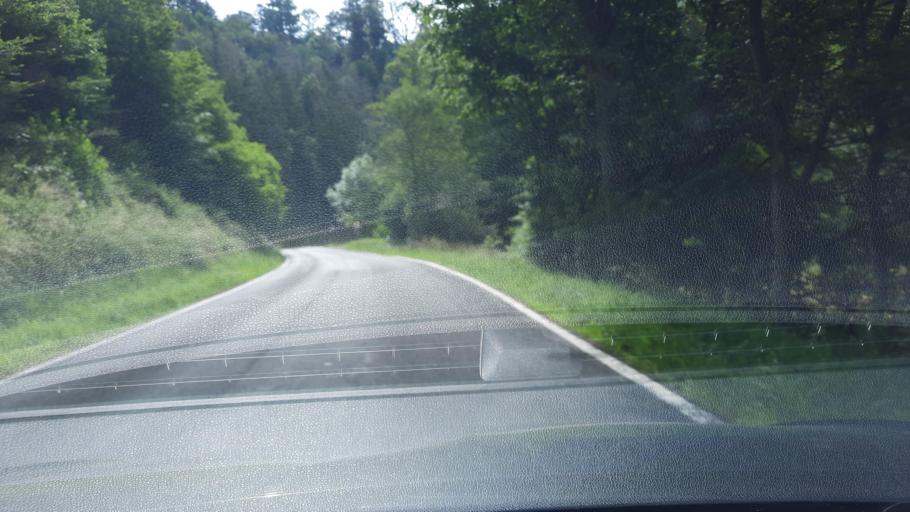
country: DE
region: Rheinland-Pfalz
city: Kempenich
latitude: 50.4141
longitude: 7.1205
